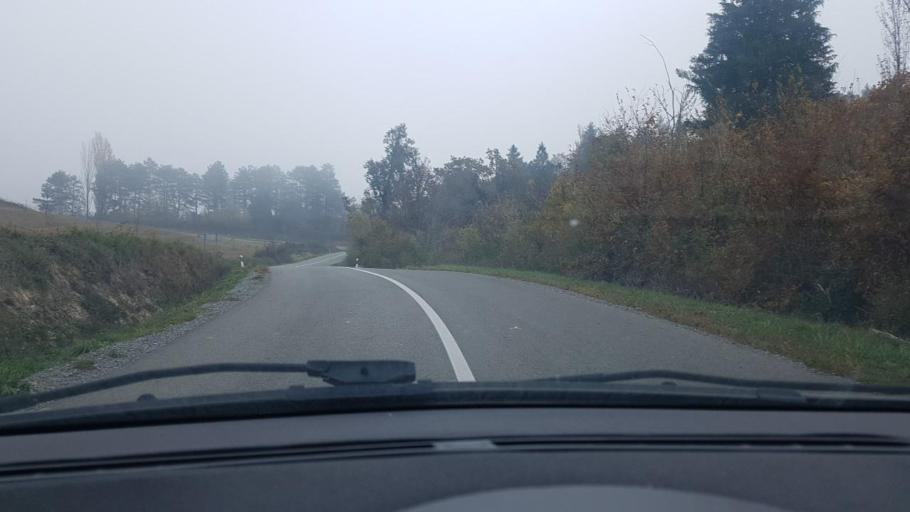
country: HR
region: Varazdinska
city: Ivanec
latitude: 46.1423
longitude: 16.1615
